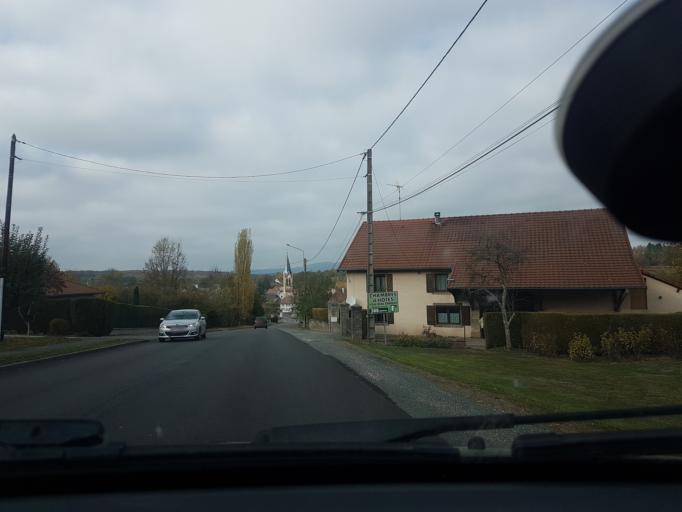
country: FR
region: Franche-Comte
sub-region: Departement de la Haute-Saone
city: Frahier-et-Chatebier
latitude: 47.6565
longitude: 6.7508
